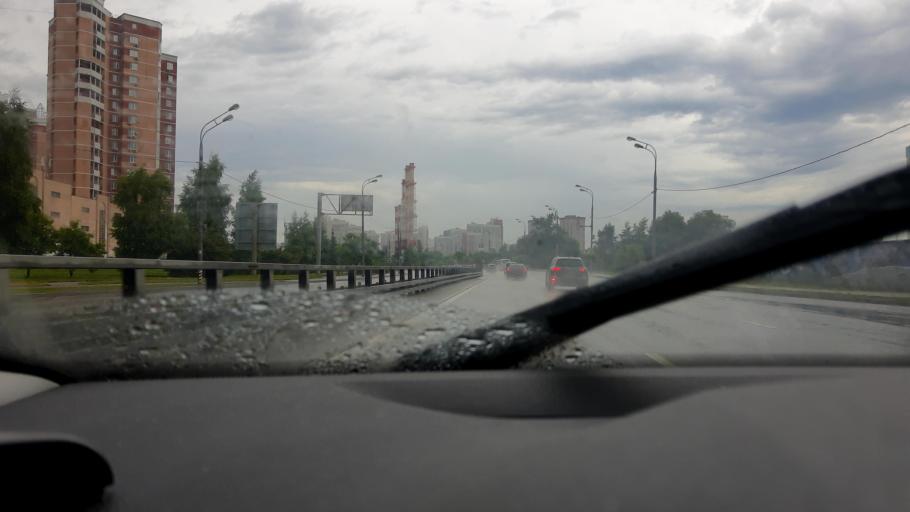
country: RU
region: Moscow
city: Khimki
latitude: 55.8900
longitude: 37.4044
